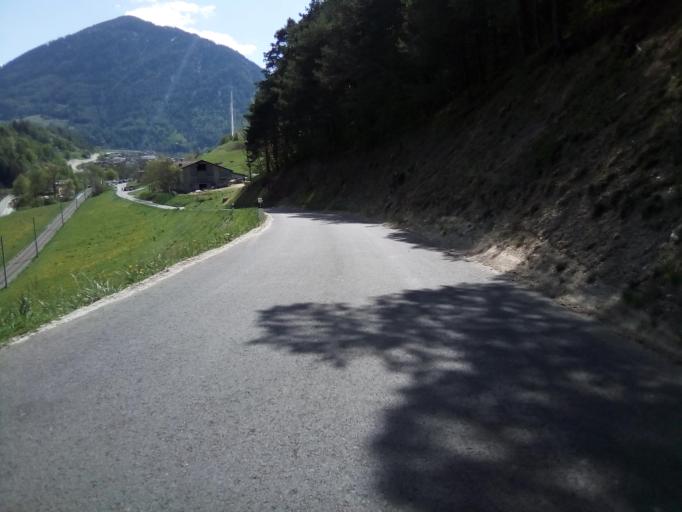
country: CH
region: Valais
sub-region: Entremont District
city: Orsieres
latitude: 46.0413
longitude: 7.1459
